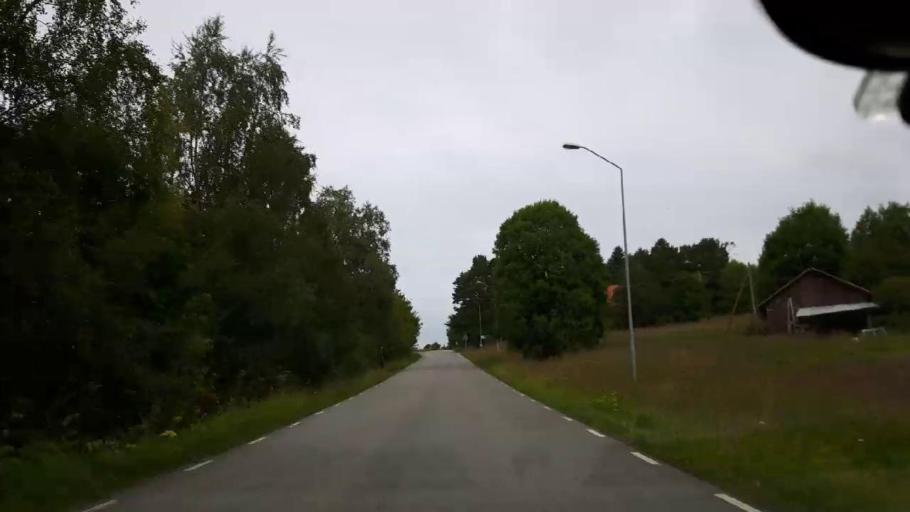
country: SE
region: Jaemtland
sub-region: OEstersunds Kommun
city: Ostersund
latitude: 63.1653
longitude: 14.5281
